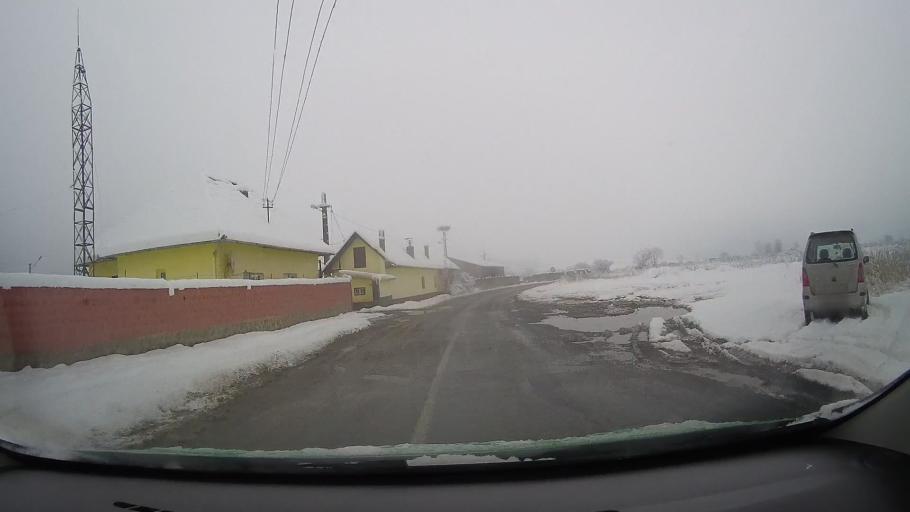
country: RO
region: Sibiu
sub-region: Comuna Orlat
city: Orlat
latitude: 45.7820
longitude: 23.9442
